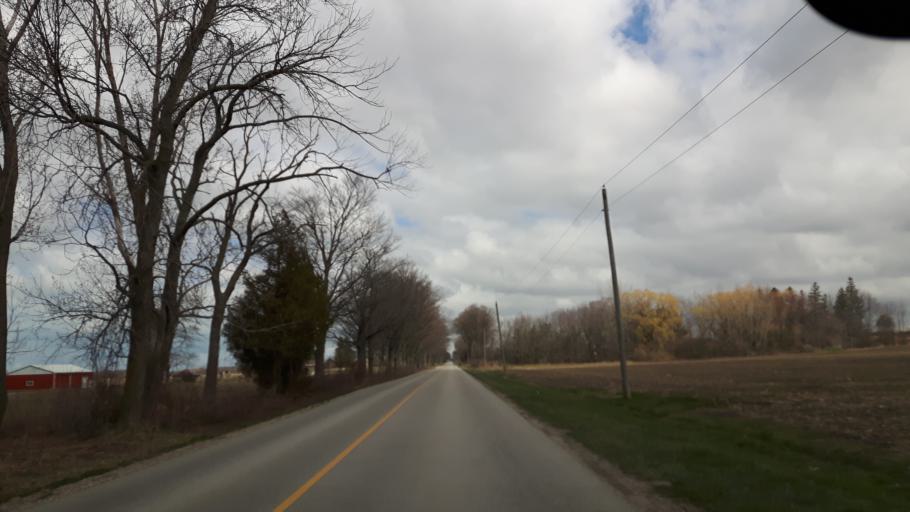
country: CA
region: Ontario
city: Goderich
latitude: 43.6908
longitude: -81.6848
